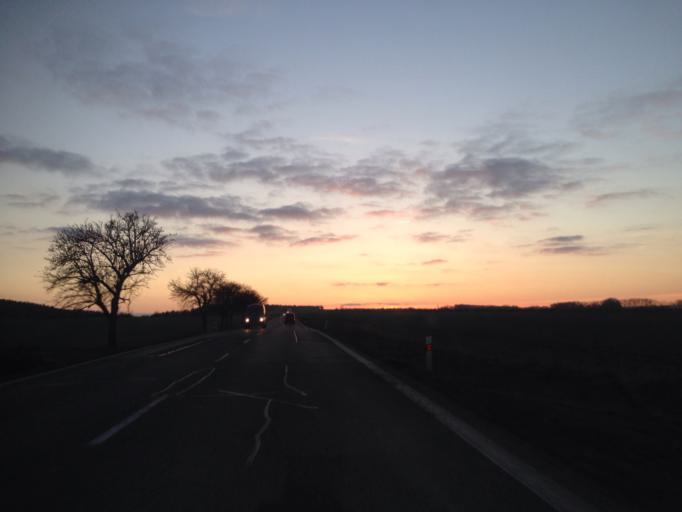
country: CZ
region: Central Bohemia
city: Rakovnik
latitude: 50.1707
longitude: 13.7082
